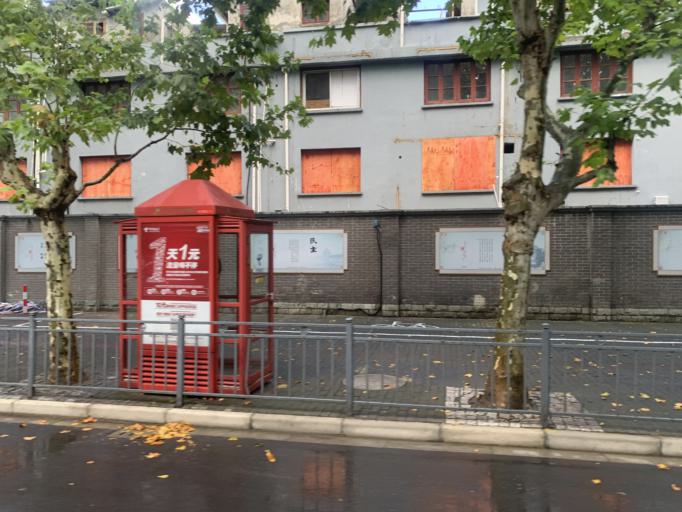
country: CN
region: Shanghai Shi
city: Luwan
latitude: 31.2135
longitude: 121.4733
